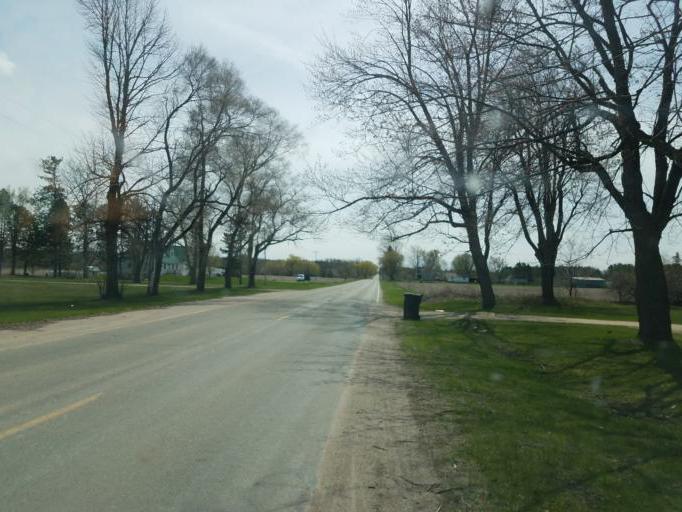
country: US
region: Michigan
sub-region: Isabella County
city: Mount Pleasant
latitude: 43.6697
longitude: -84.7081
